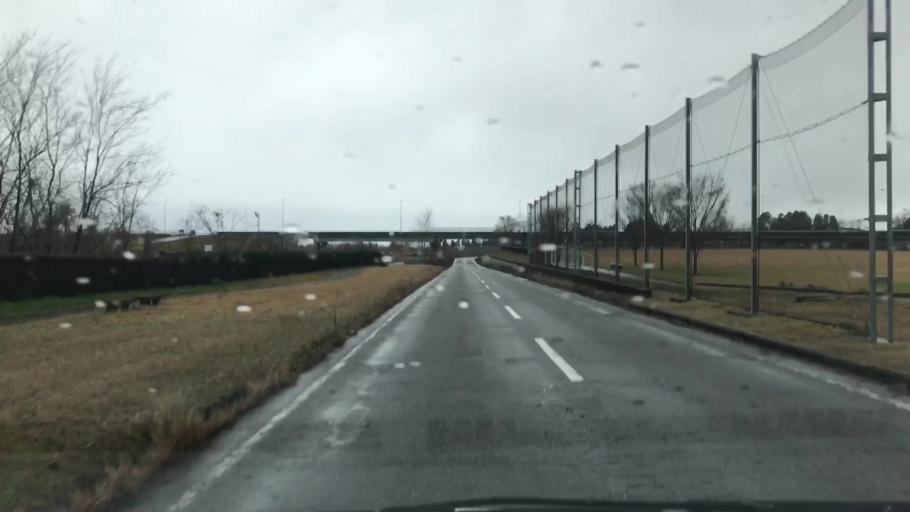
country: JP
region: Toyama
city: Kamiichi
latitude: 36.6248
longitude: 137.3017
